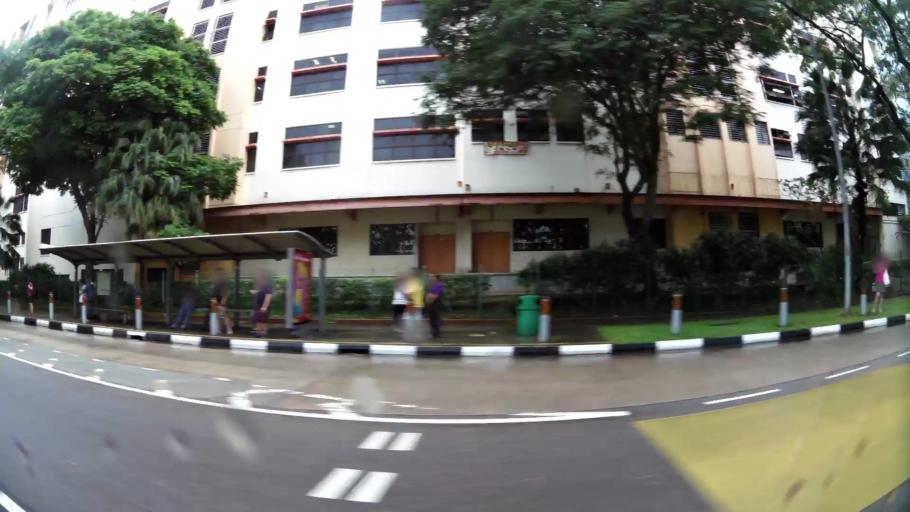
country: SG
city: Singapore
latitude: 1.3785
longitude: 103.8706
